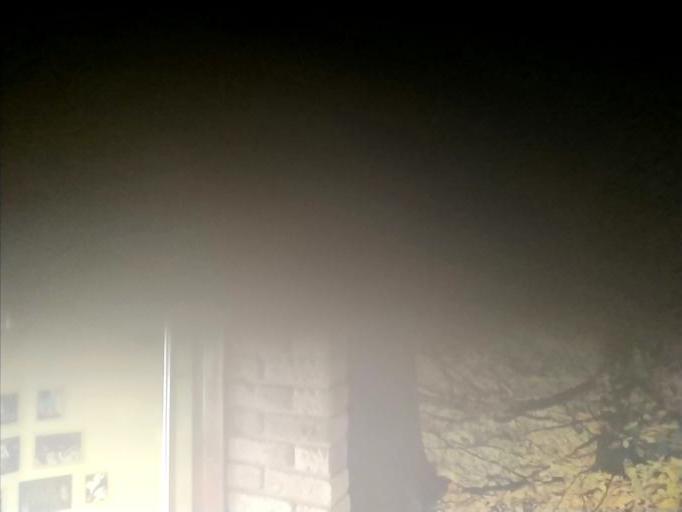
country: RU
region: Kaluga
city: Yukhnov
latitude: 54.6764
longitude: 35.0606
